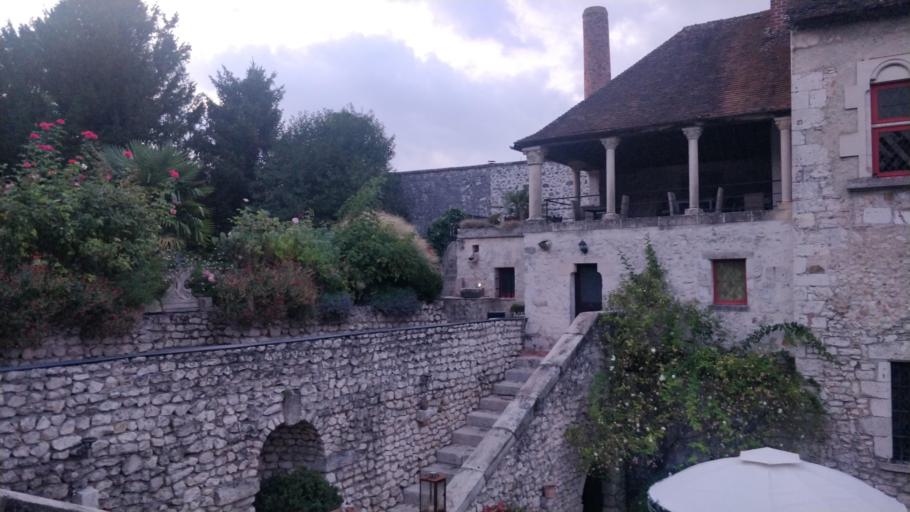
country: FR
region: Ile-de-France
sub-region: Departement de Seine-et-Marne
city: Provins
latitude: 48.5616
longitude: 3.2956
